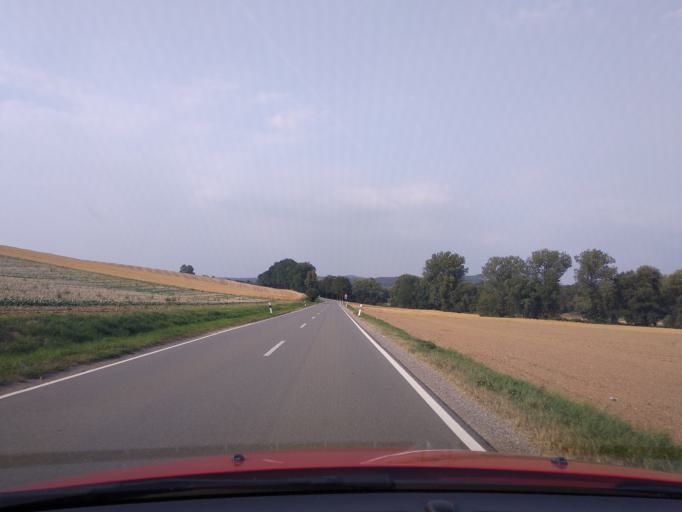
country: DE
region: Hesse
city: Liebenau
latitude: 51.4487
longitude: 9.3071
